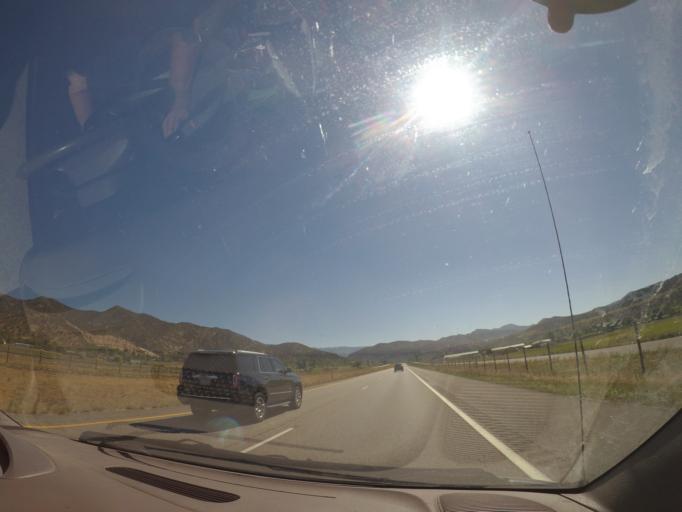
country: US
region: Colorado
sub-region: Garfield County
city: New Castle
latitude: 39.5541
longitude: -107.5776
